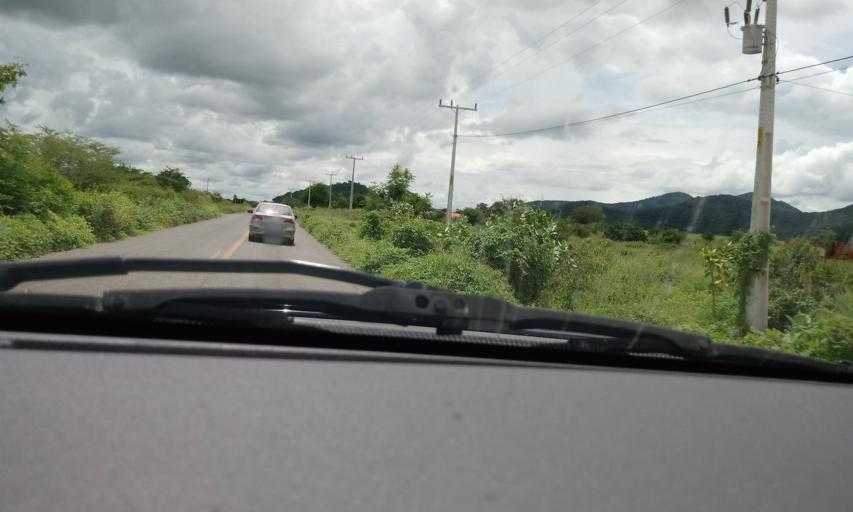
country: BR
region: Bahia
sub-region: Guanambi
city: Guanambi
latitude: -14.1216
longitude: -42.8547
